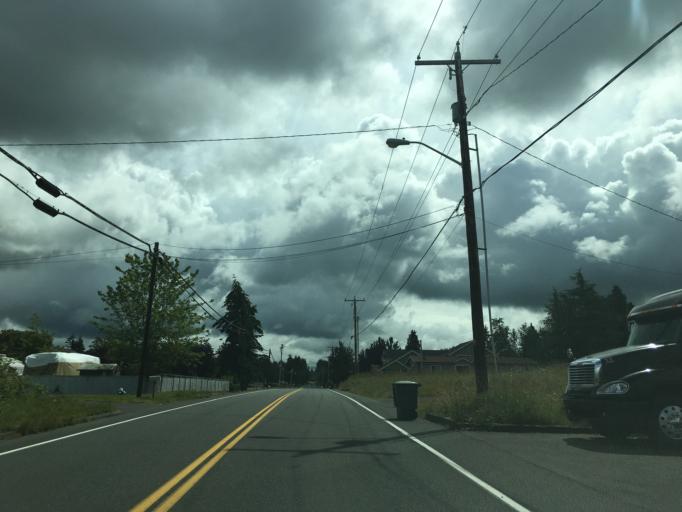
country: US
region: Washington
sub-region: Whatcom County
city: Birch Bay
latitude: 48.9177
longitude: -122.7407
